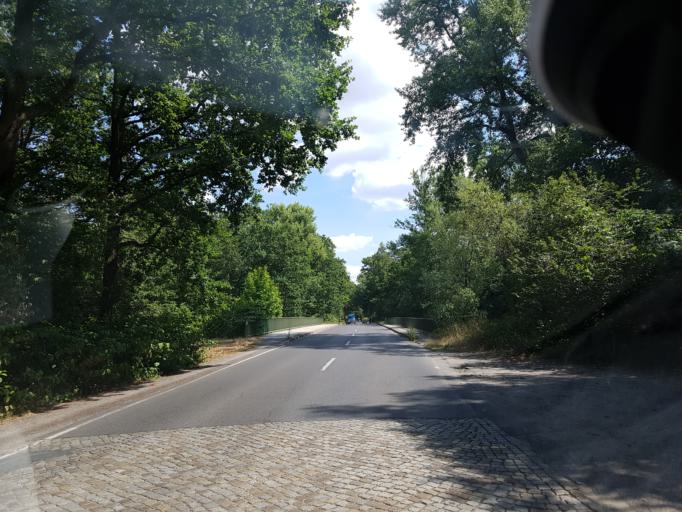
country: DE
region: Brandenburg
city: Cottbus
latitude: 51.7203
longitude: 14.3558
